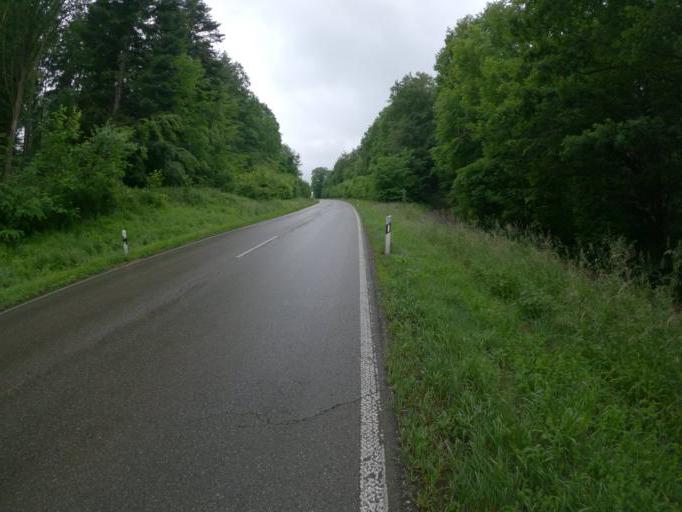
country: DE
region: Baden-Wuerttemberg
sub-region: Regierungsbezirk Stuttgart
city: Adelberg
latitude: 48.7521
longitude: 9.6135
